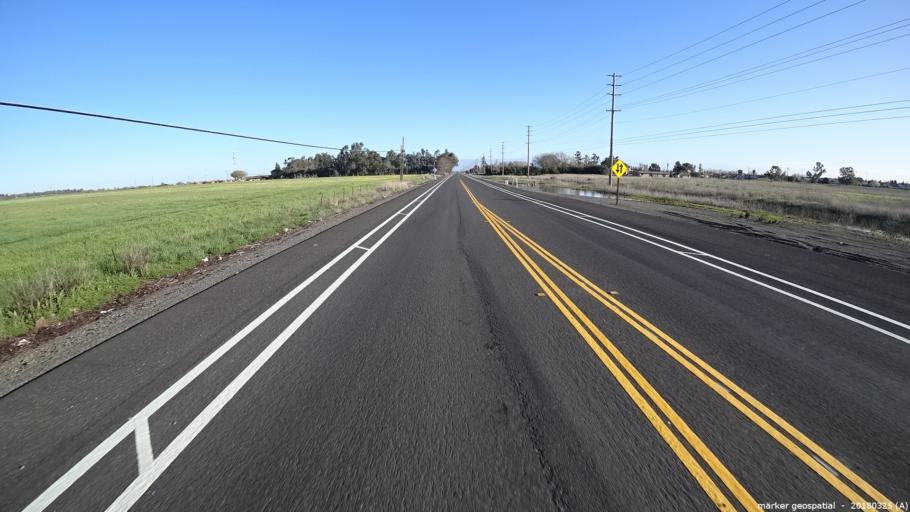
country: US
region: California
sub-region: Yolo County
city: West Sacramento
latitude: 38.6316
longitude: -121.5396
